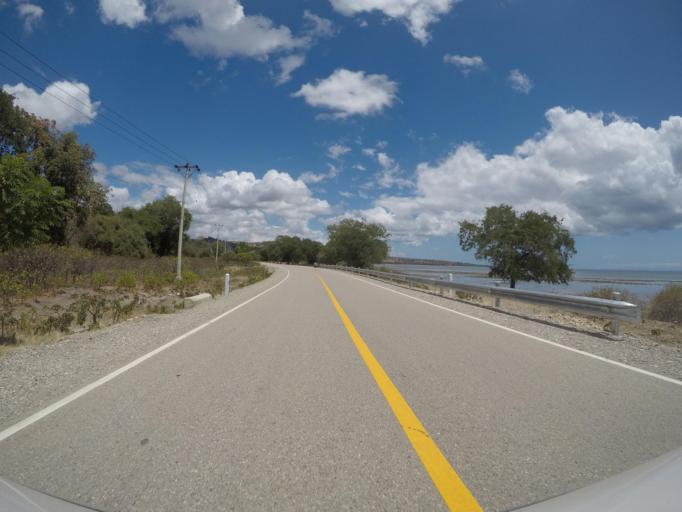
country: TL
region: Lautem
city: Lospalos
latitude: -8.4190
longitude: 126.7755
